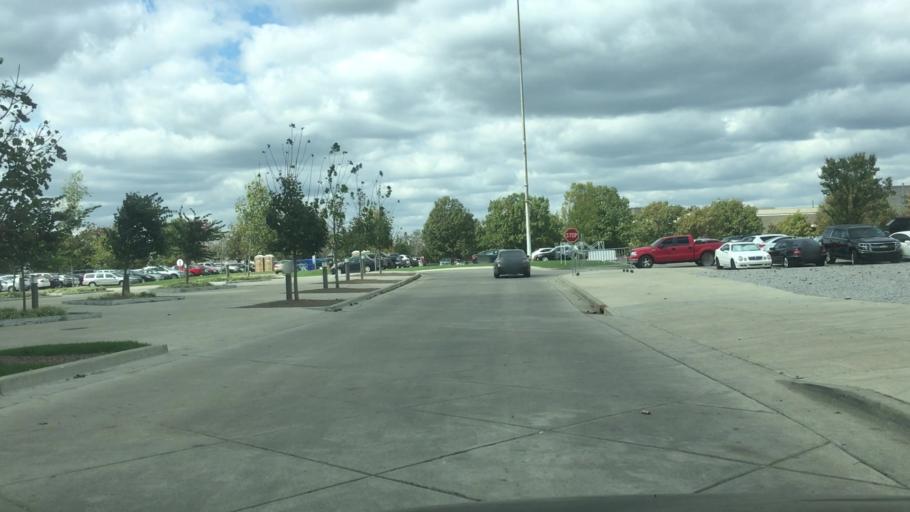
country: US
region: Kentucky
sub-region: Fayette County
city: Mount Vernon
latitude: 38.0241
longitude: -84.5051
